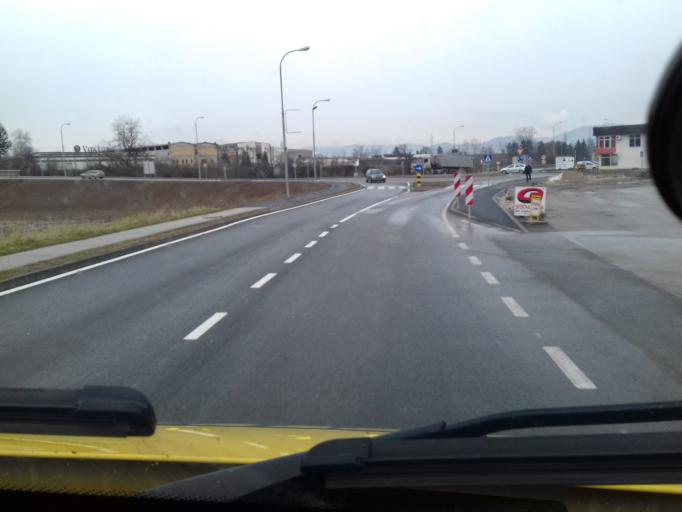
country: BA
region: Federation of Bosnia and Herzegovina
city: Visoko
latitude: 43.9992
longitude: 18.1674
